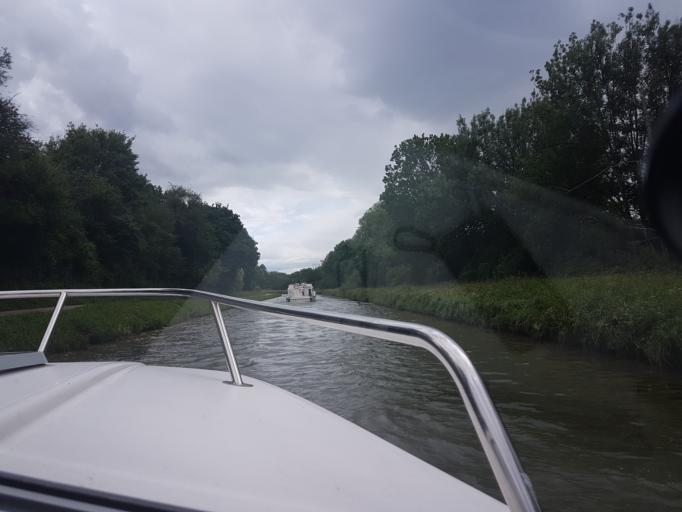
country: FR
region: Bourgogne
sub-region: Departement de l'Yonne
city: Vermenton
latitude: 47.5535
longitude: 3.6322
